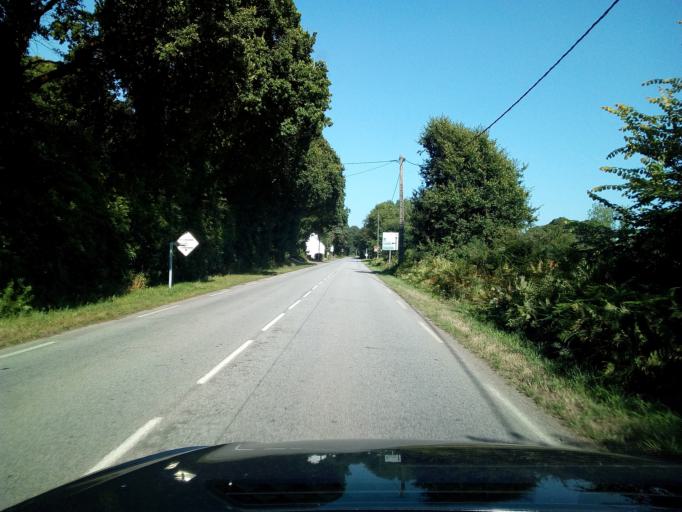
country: FR
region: Brittany
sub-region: Departement du Finistere
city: Landivisiau
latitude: 48.4990
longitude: -4.0968
